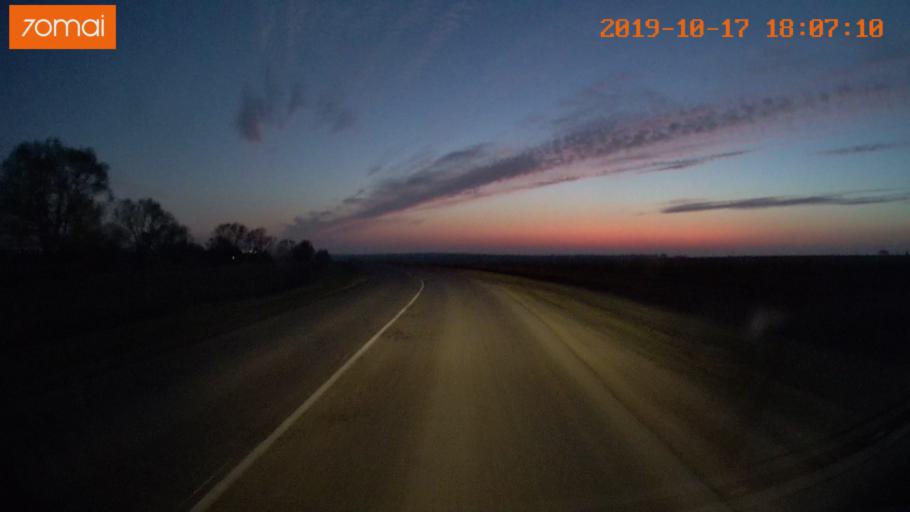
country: RU
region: Tula
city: Kurkino
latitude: 53.4458
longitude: 38.6583
